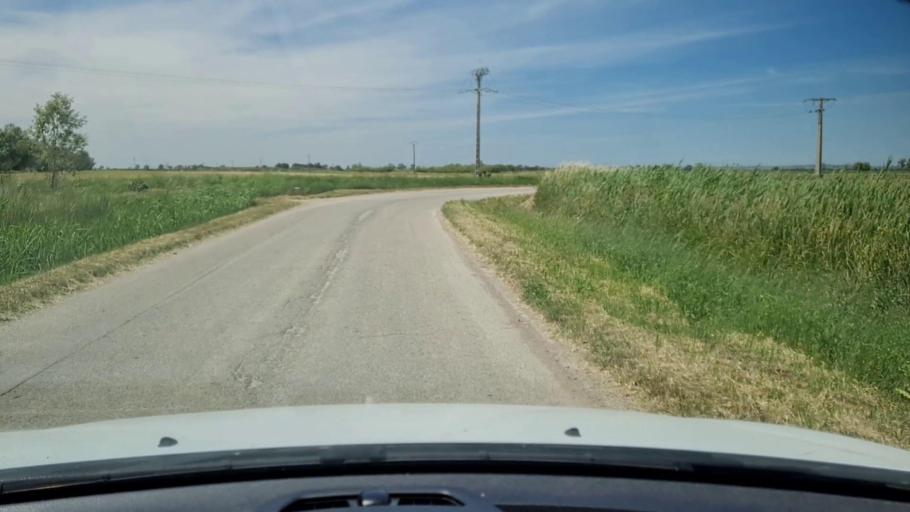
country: FR
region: Languedoc-Roussillon
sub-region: Departement du Gard
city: Saint-Gilles
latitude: 43.6103
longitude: 4.4265
